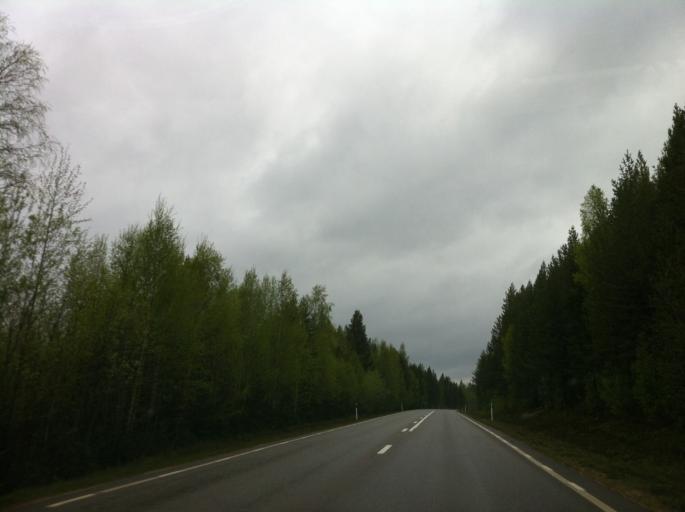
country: SE
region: Jaemtland
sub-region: Harjedalens Kommun
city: Sveg
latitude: 62.1008
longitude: 14.2146
